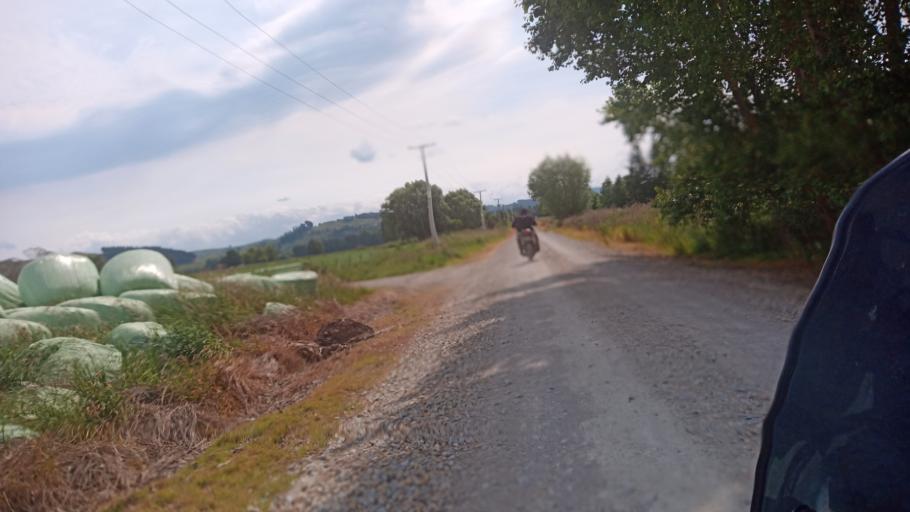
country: NZ
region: Gisborne
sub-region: Gisborne District
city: Gisborne
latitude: -38.4692
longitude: 177.8587
